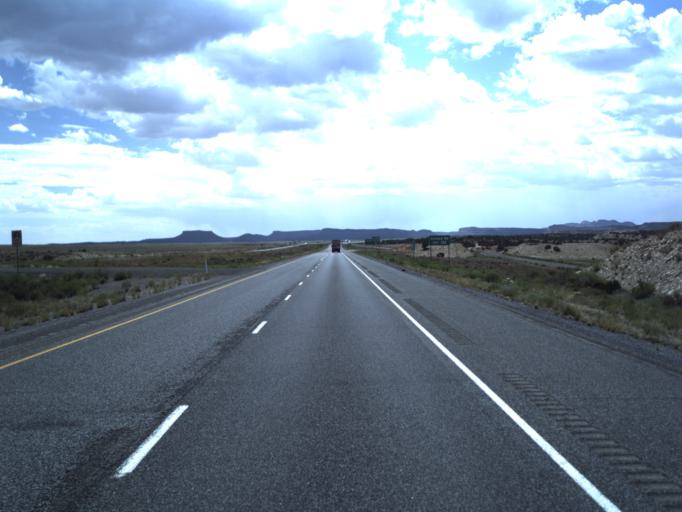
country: US
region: Utah
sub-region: Emery County
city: Castle Dale
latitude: 38.8864
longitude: -110.6514
